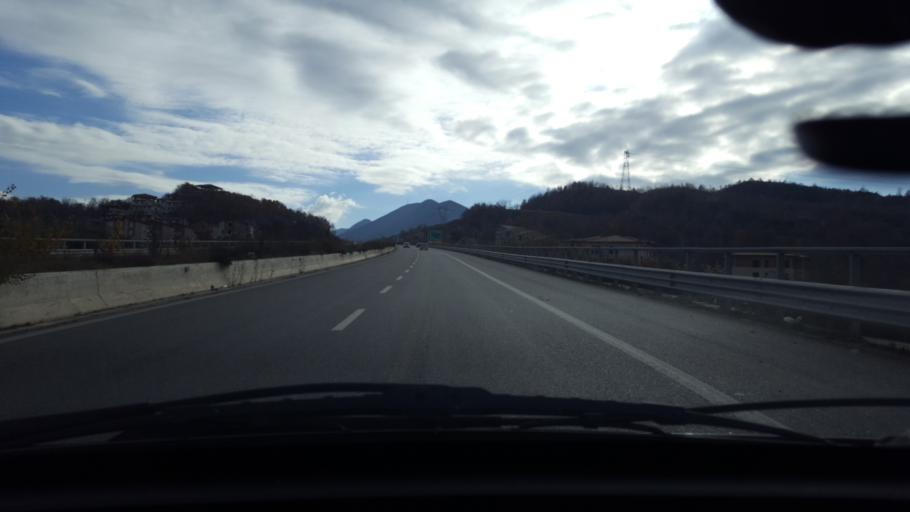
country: AL
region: Tirane
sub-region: Rrethi i Tiranes
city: Petrele
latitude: 41.2743
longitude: 19.8576
